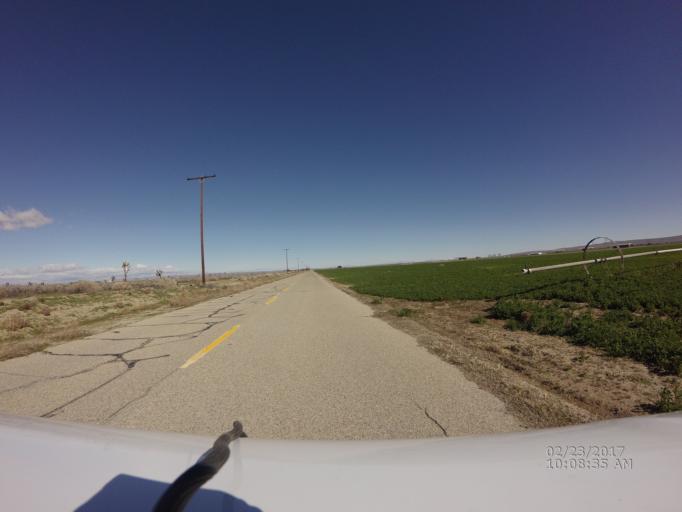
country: US
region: California
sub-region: Los Angeles County
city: Lake Los Angeles
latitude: 34.7072
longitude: -117.9342
